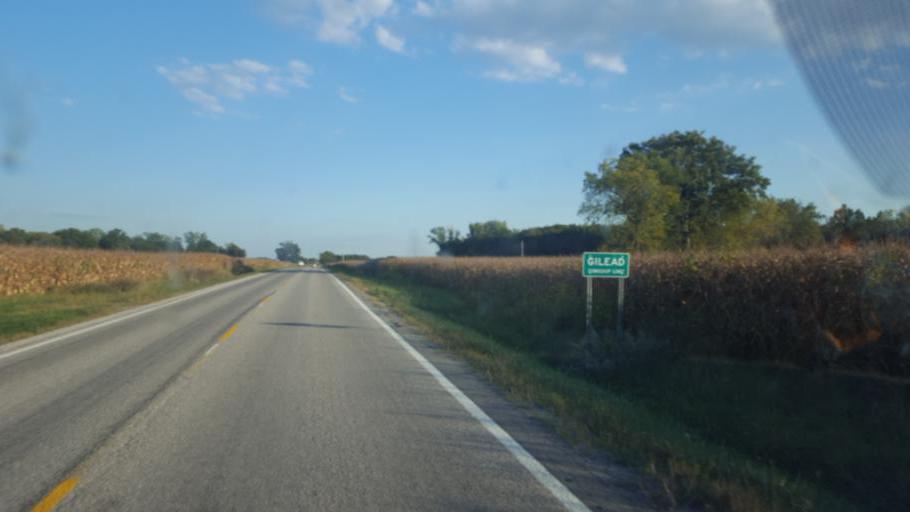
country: US
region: Ohio
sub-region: Morrow County
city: Mount Gilead
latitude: 40.5674
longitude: -82.8816
